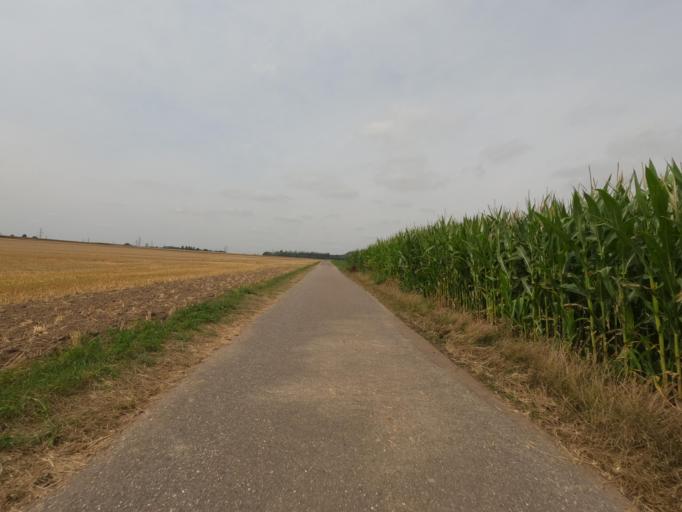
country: DE
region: North Rhine-Westphalia
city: Siersdorf
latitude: 50.9109
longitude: 6.2492
